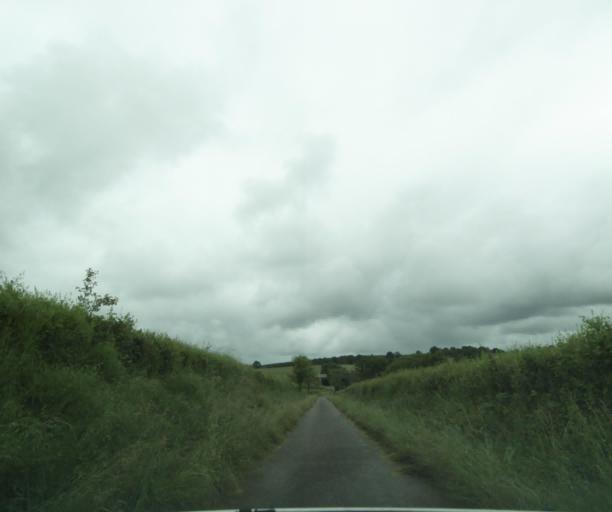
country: FR
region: Bourgogne
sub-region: Departement de Saone-et-Loire
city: Charolles
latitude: 46.4545
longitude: 4.3511
